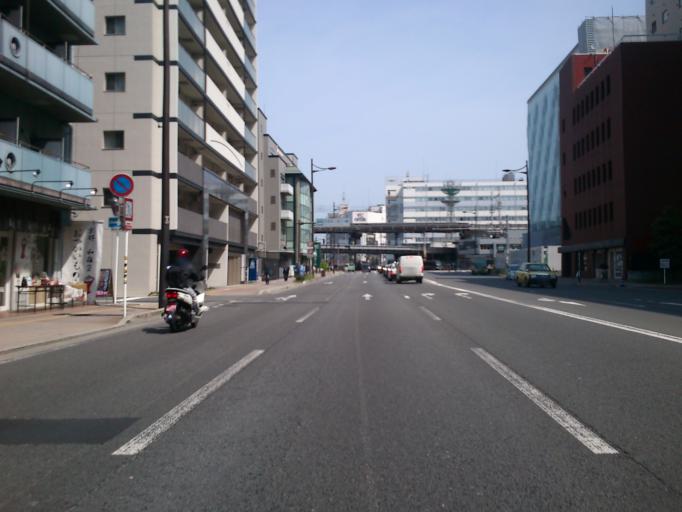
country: JP
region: Kyoto
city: Kyoto
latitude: 34.9829
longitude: 135.7537
